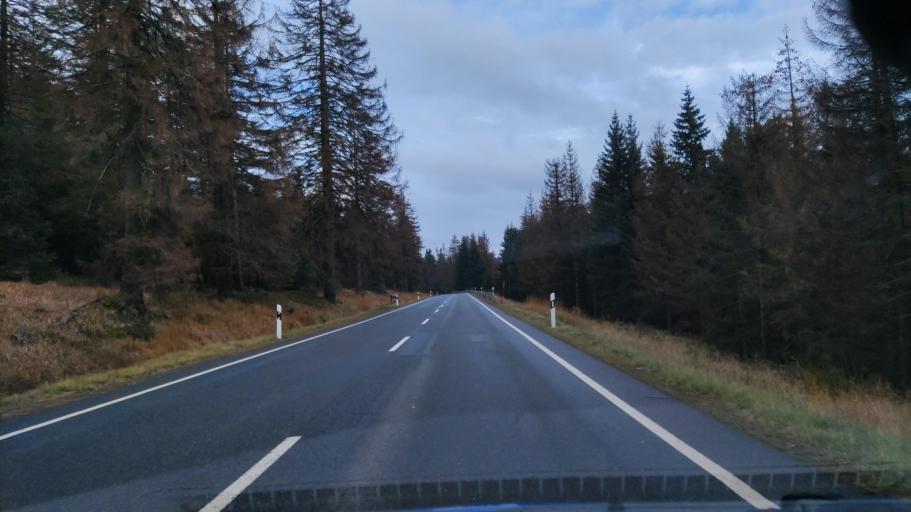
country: DE
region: Lower Saxony
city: Altenau
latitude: 51.7676
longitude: 10.4710
